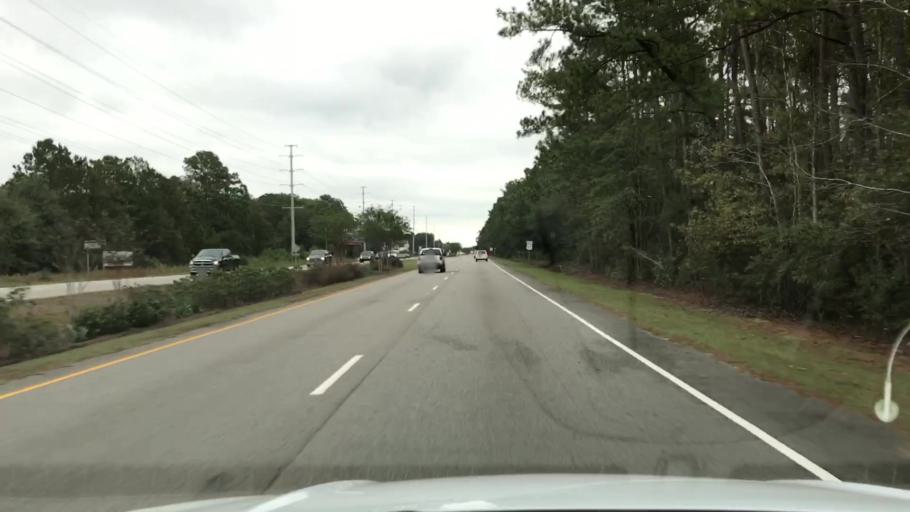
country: US
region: South Carolina
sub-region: Georgetown County
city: Georgetown
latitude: 33.4210
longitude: -79.1731
